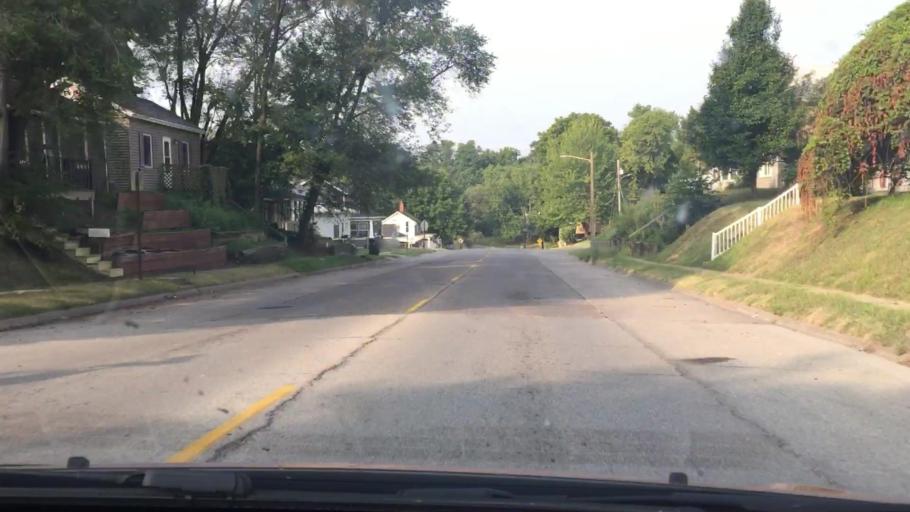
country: US
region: Iowa
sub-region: Muscatine County
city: Muscatine
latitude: 41.4224
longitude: -91.0570
